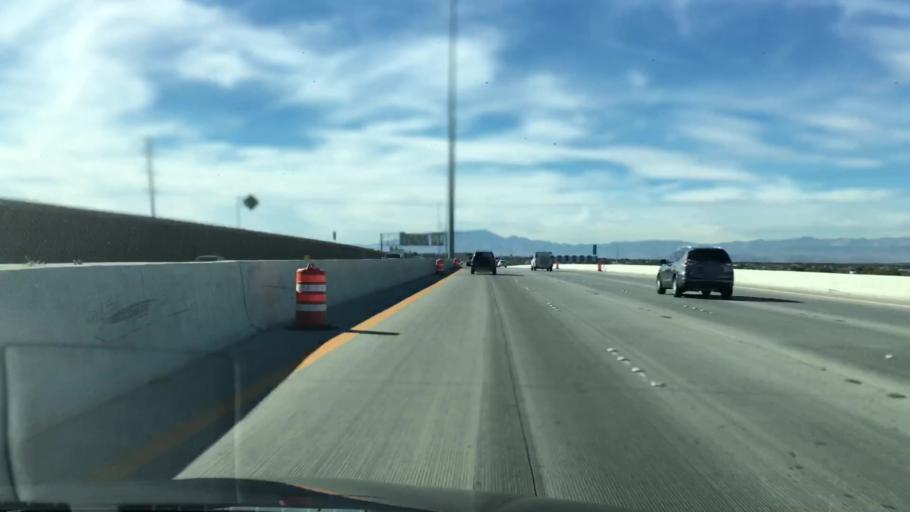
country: US
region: Nevada
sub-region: Clark County
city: Henderson
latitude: 36.0321
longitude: -115.0278
